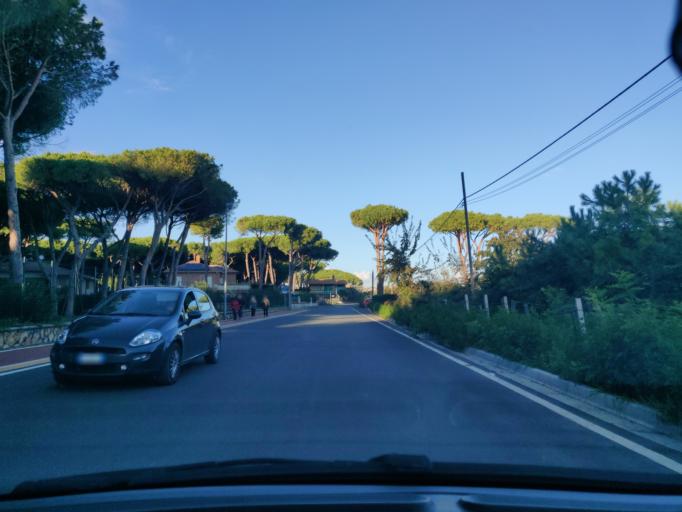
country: IT
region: Latium
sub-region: Provincia di Viterbo
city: Tarquinia
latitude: 42.2156
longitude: 11.7105
